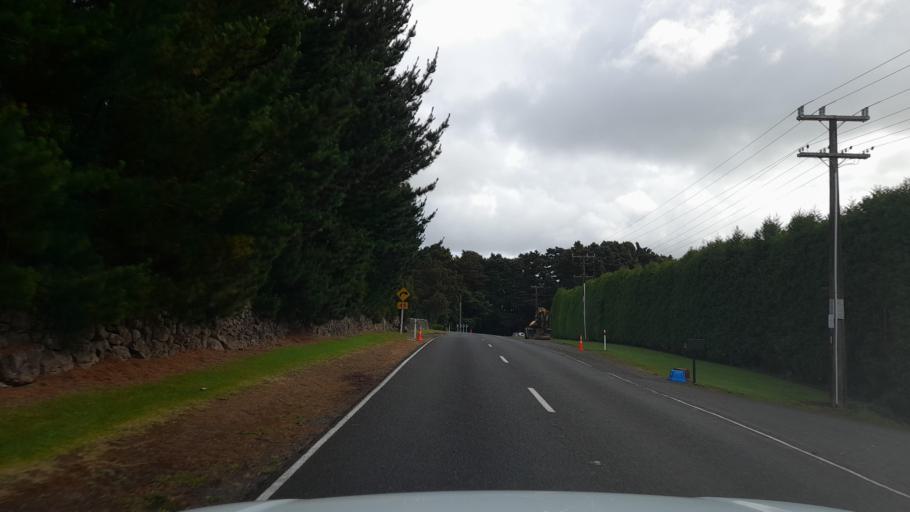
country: NZ
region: Northland
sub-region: Whangarei
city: Maungatapere
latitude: -35.7517
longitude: 174.2518
